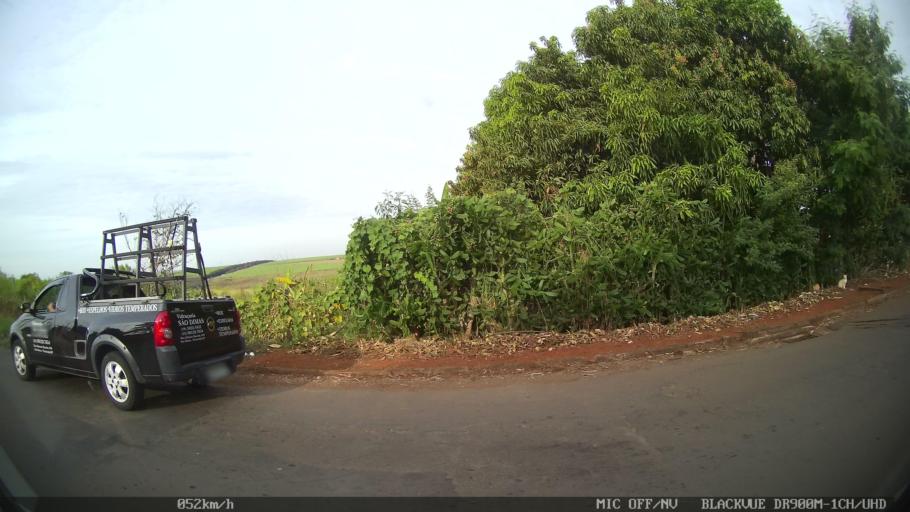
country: BR
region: Sao Paulo
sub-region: Piracicaba
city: Piracicaba
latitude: -22.7279
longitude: -47.5861
